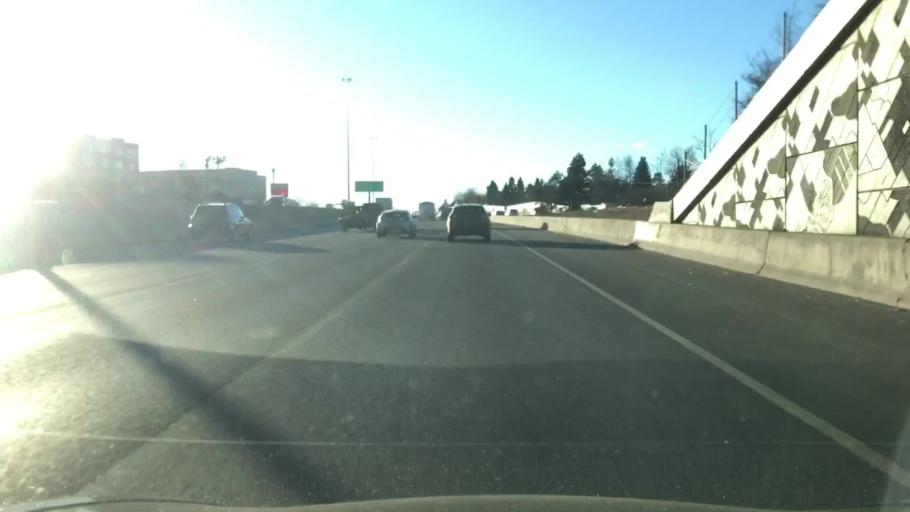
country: US
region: Colorado
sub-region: Arapahoe County
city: Cherry Hills Village
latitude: 39.6536
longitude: -104.9159
